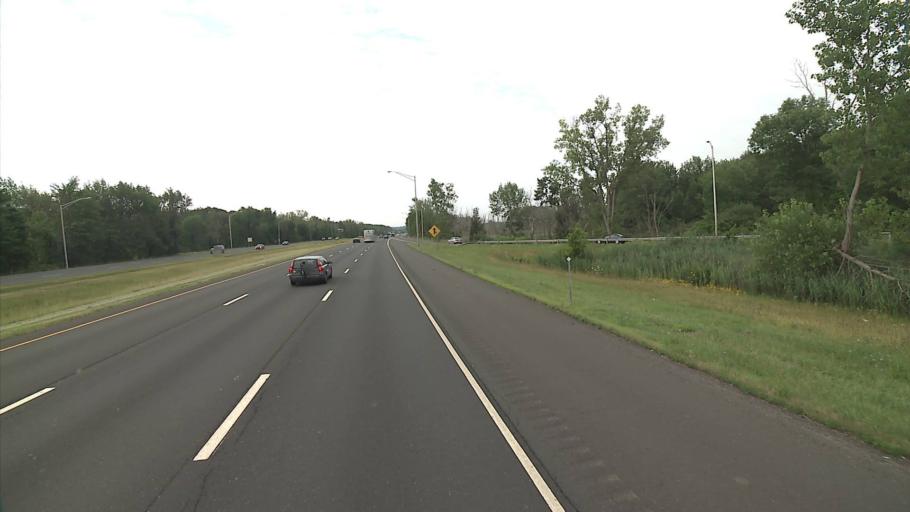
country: US
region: Connecticut
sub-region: Hartford County
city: Farmington
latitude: 41.7040
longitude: -72.8040
